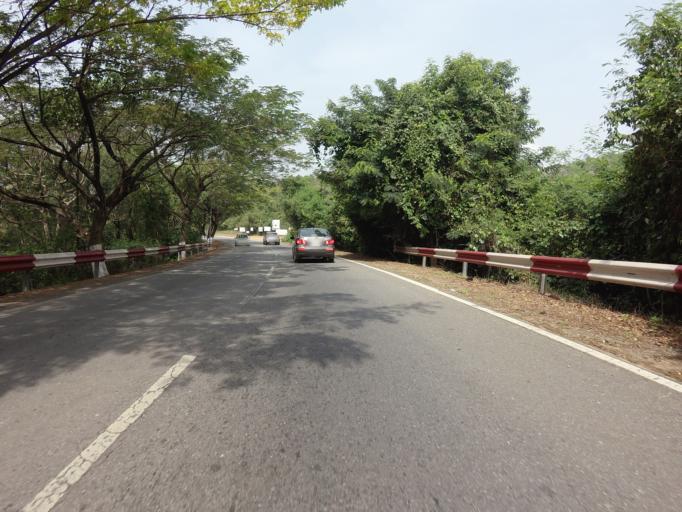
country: GH
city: Akropong
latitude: 6.2701
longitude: 0.0578
